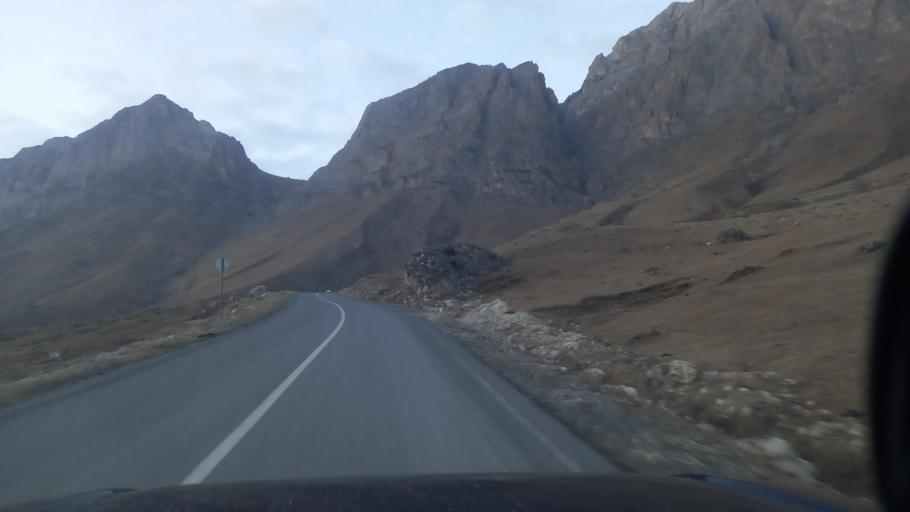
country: RU
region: Ingushetiya
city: Dzhayrakh
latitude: 42.8214
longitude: 44.8266
